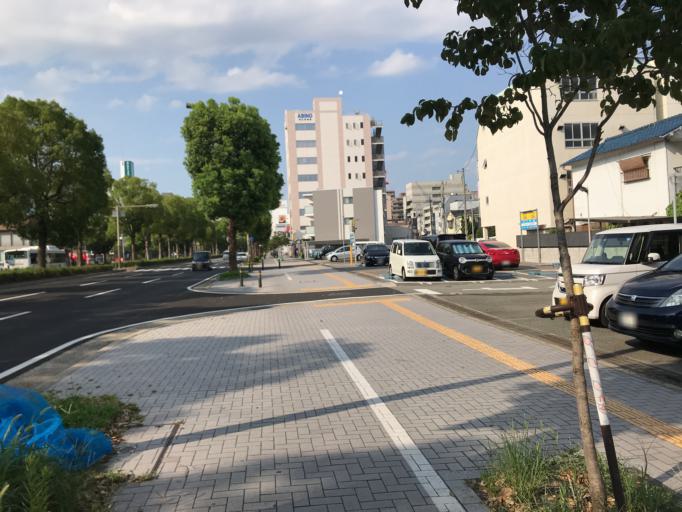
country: JP
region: Hyogo
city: Himeji
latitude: 34.8174
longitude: 134.6853
